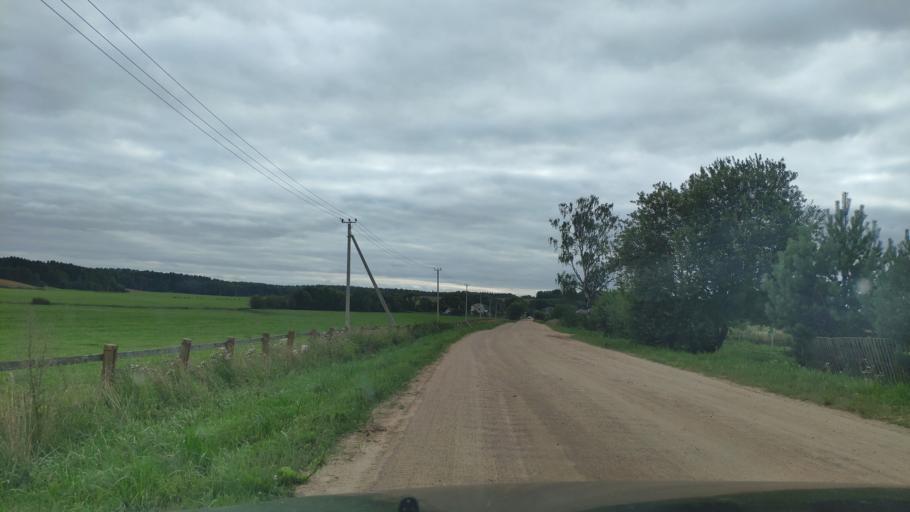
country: BY
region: Minsk
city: Khatsyezhyna
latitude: 53.9296
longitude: 27.2659
